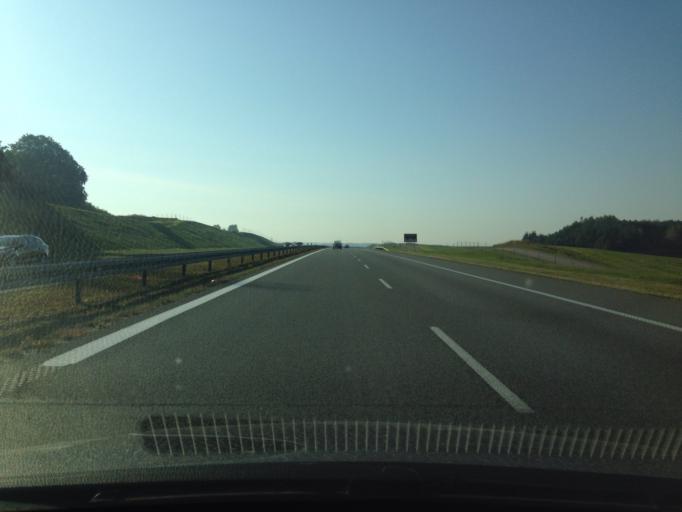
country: PL
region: Pomeranian Voivodeship
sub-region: Powiat tczewski
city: Subkowy
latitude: 54.0451
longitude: 18.6714
